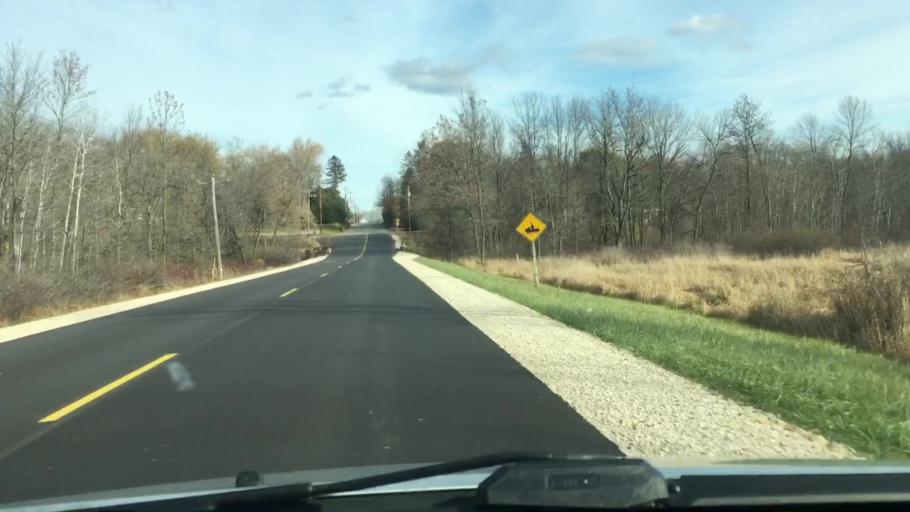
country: US
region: Wisconsin
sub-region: Kewaunee County
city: Algoma
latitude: 44.6900
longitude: -87.4886
